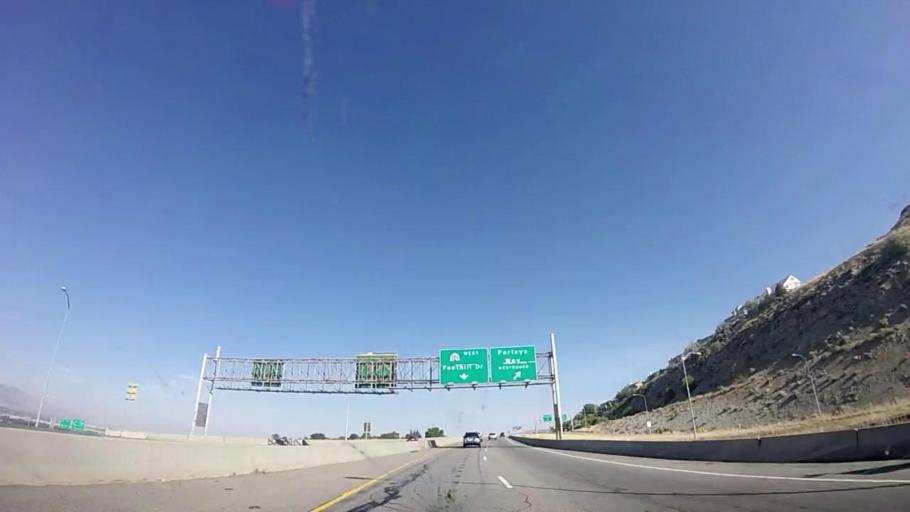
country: US
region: Utah
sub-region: Salt Lake County
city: East Millcreek
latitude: 40.7132
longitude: -111.8057
